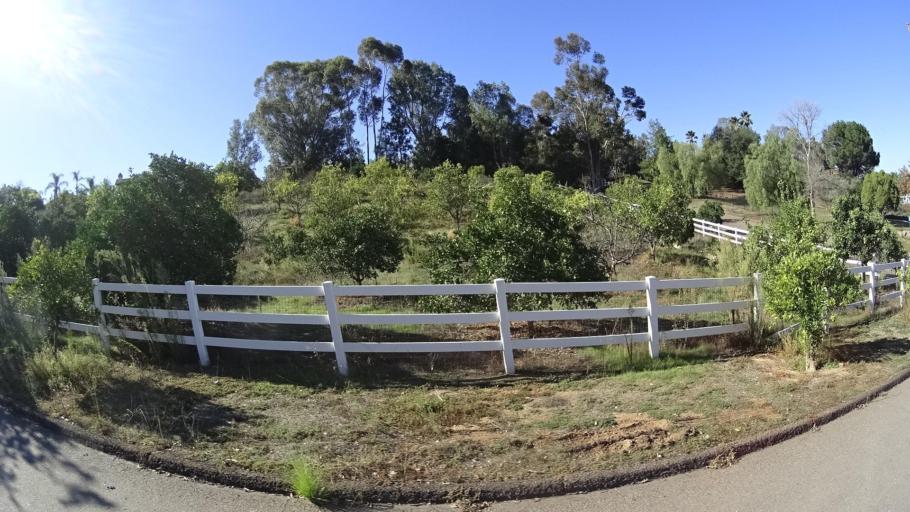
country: US
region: California
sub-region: San Diego County
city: Jamul
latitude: 32.7171
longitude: -116.8486
